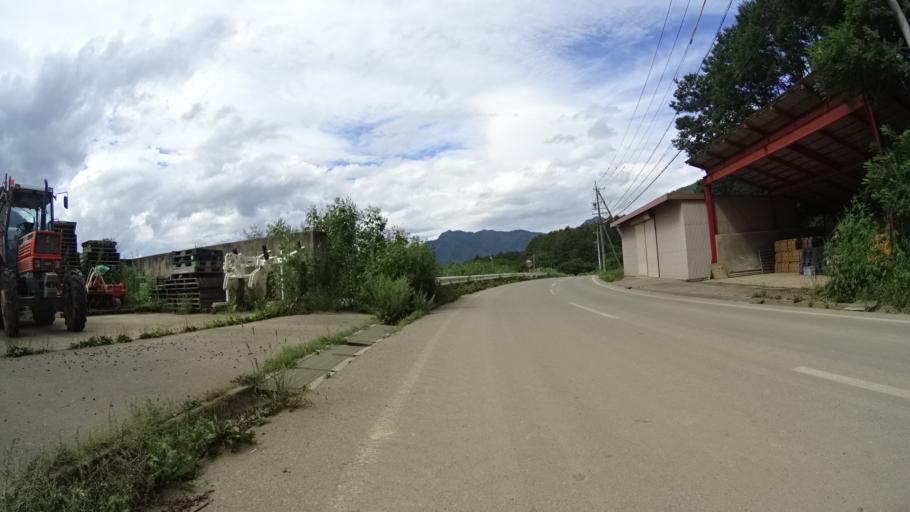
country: JP
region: Yamanashi
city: Nirasaki
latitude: 35.9423
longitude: 138.5479
